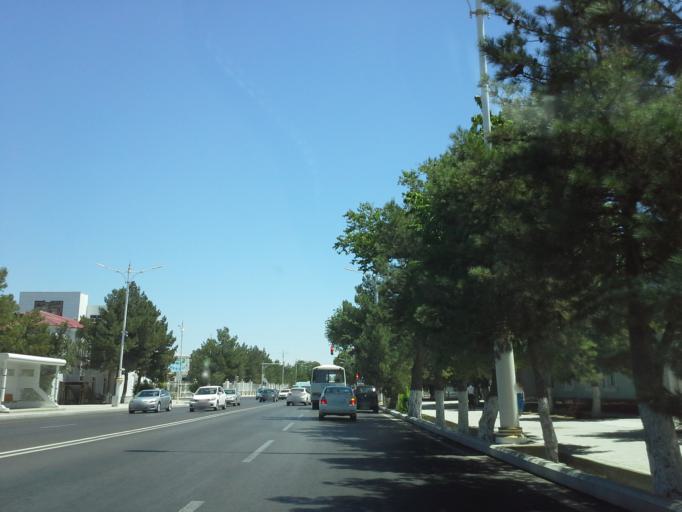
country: TM
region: Ahal
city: Ashgabat
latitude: 37.9523
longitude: 58.3685
